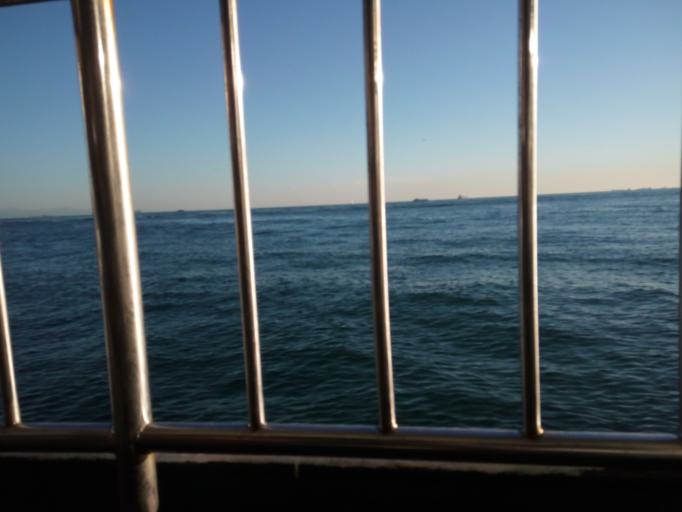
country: TR
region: Istanbul
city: UEskuedar
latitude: 40.9958
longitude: 29.0143
